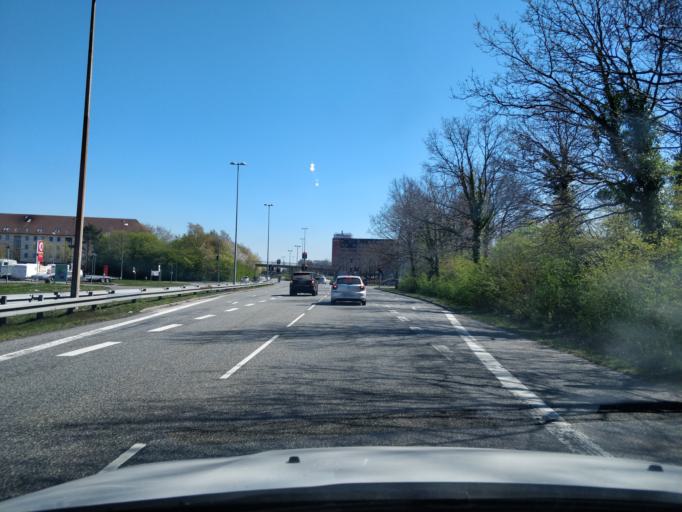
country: DK
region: Capital Region
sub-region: Ishoj Kommune
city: Ishoj
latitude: 55.6163
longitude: 12.3501
